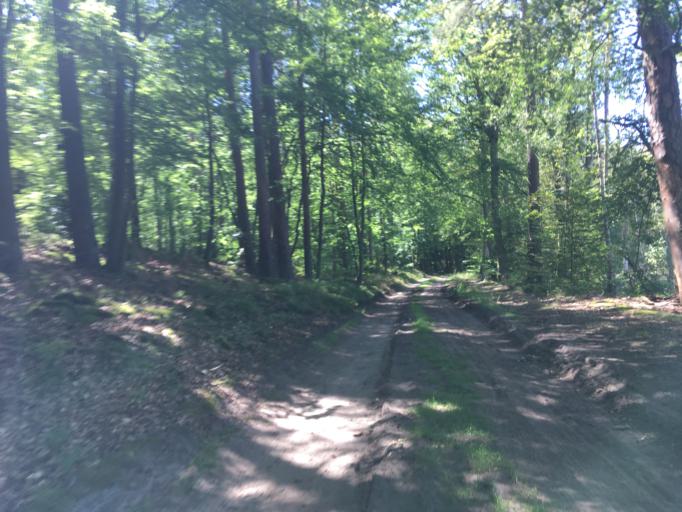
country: DE
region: Brandenburg
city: Rheinsberg
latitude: 53.1173
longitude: 13.0026
